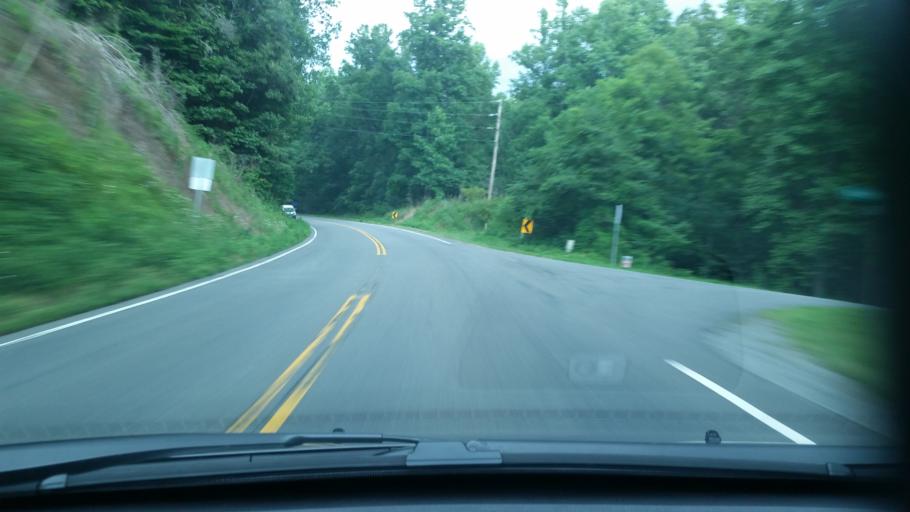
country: US
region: Virginia
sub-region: Nelson County
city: Nellysford
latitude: 37.8593
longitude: -78.8122
